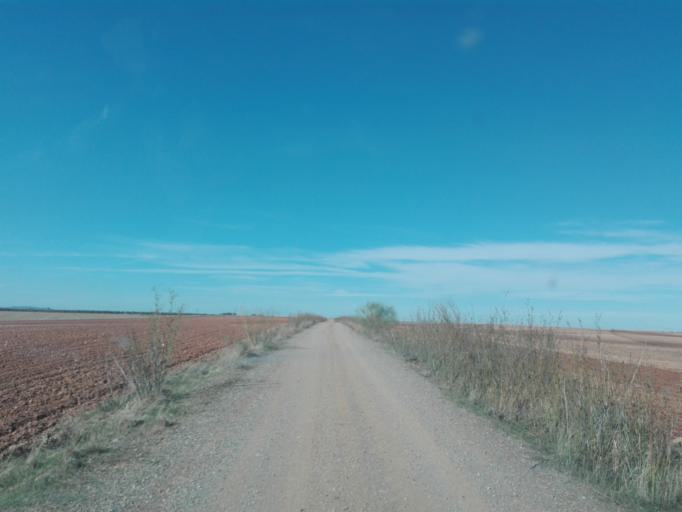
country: ES
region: Extremadura
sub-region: Provincia de Badajoz
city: Ahillones
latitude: 38.3028
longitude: -5.9324
